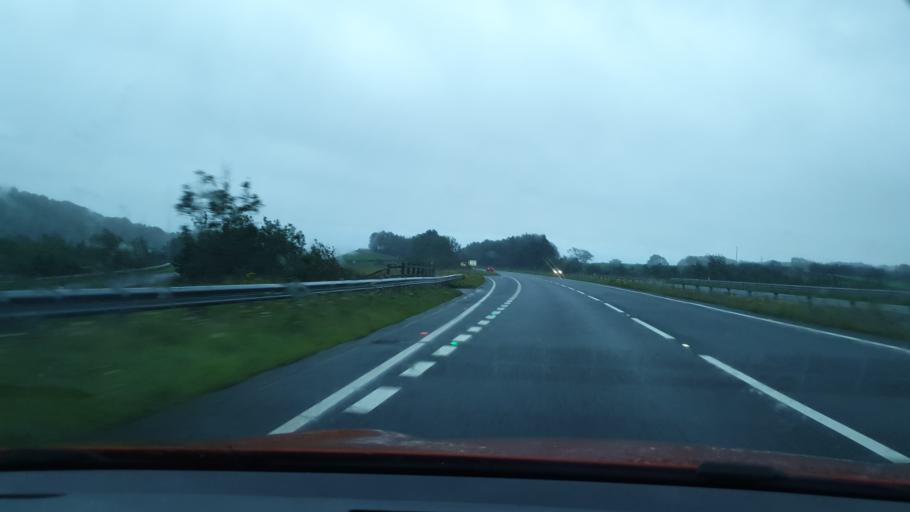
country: GB
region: England
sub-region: Cumbria
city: Grange-over-Sands
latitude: 54.2290
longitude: -2.9140
